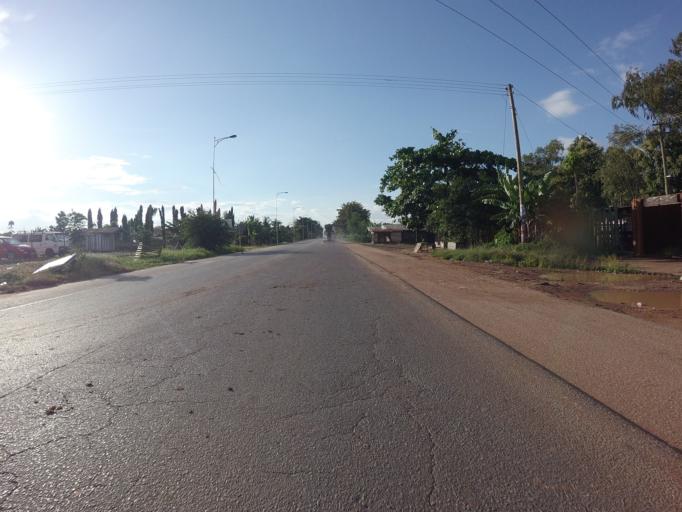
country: GH
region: Ashanti
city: Tafo
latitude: 6.9242
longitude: -1.6623
